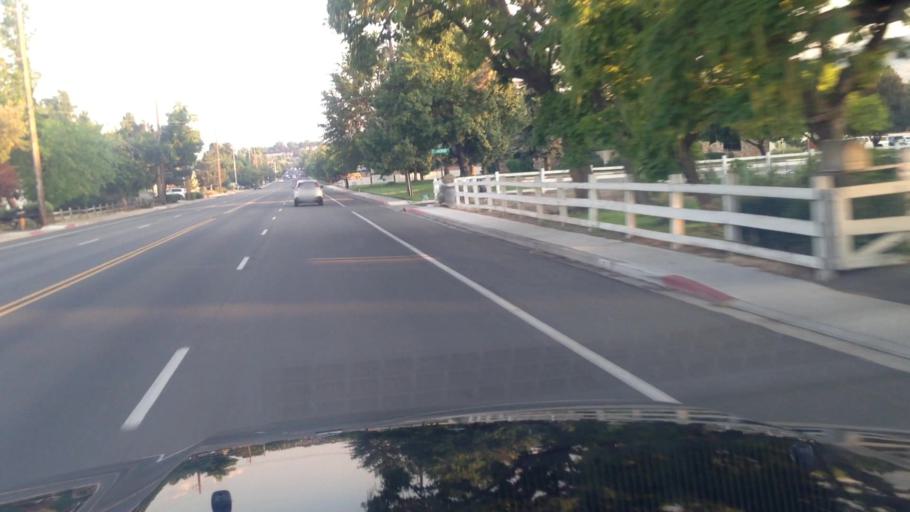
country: US
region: Nevada
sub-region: Washoe County
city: Reno
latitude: 39.4822
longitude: -119.8080
